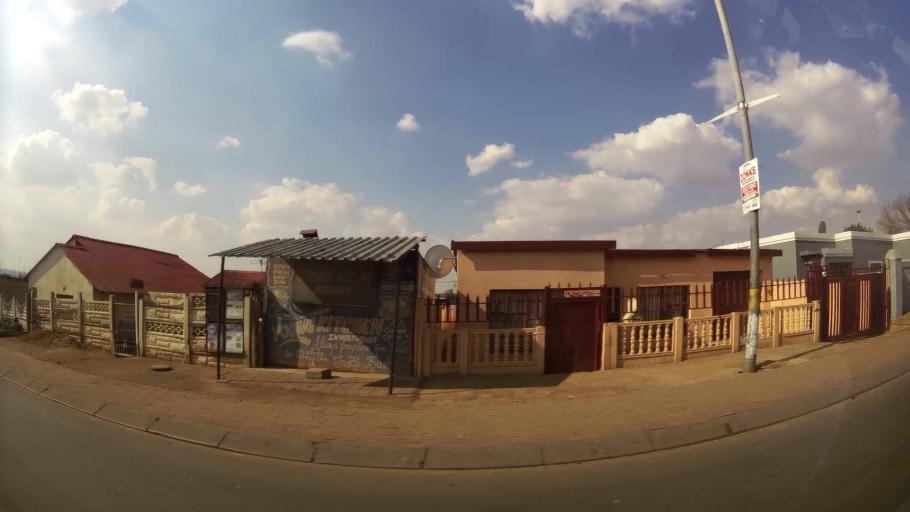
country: ZA
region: Gauteng
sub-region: Ekurhuleni Metropolitan Municipality
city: Germiston
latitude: -26.3155
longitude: 28.1574
